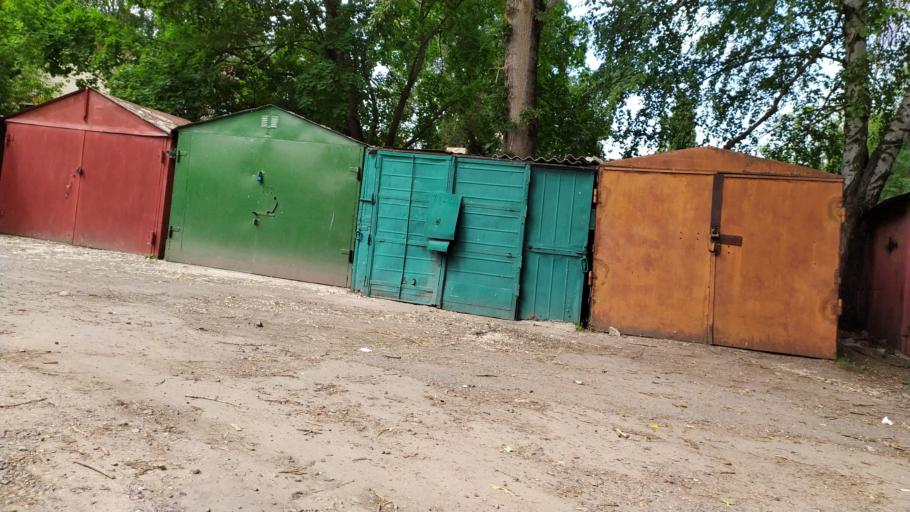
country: RU
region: Kursk
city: Kursk
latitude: 51.6656
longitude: 36.1506
